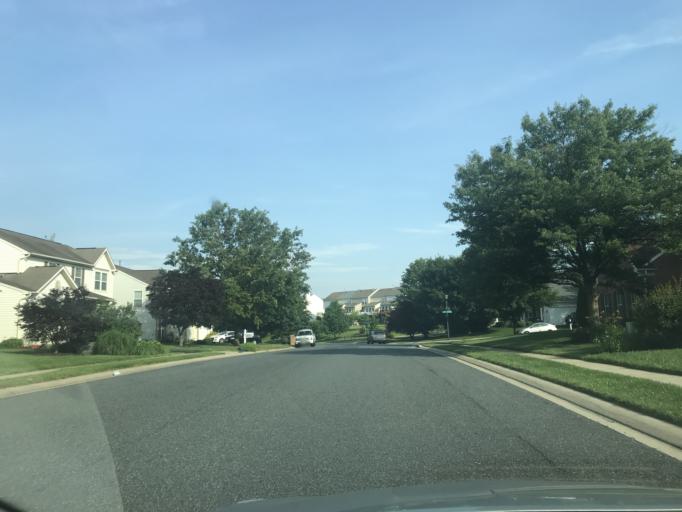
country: US
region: Maryland
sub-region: Harford County
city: North Bel Air
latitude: 39.5531
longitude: -76.3557
